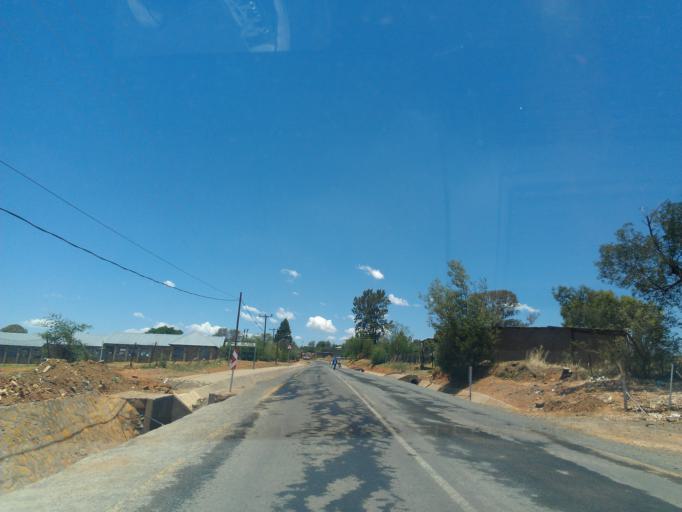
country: LS
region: Berea
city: Teyateyaneng
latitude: -29.1147
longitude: 27.9694
